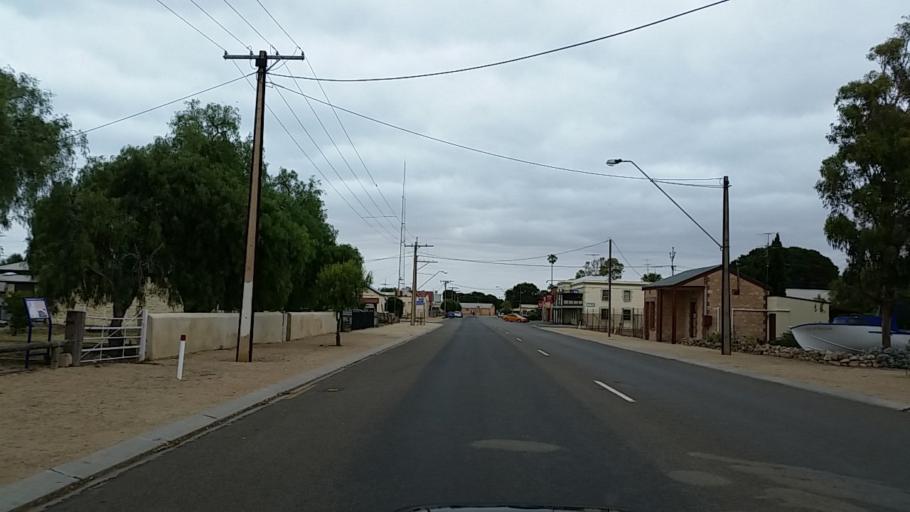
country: AU
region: South Australia
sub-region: Wakefield
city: Balaklava
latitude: -34.1851
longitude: 138.1496
